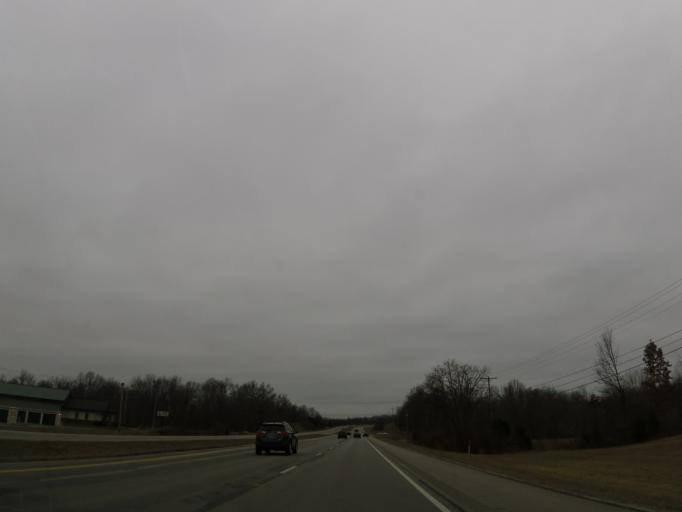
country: US
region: Kentucky
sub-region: Franklin County
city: Frankfort
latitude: 38.1457
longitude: -84.8995
